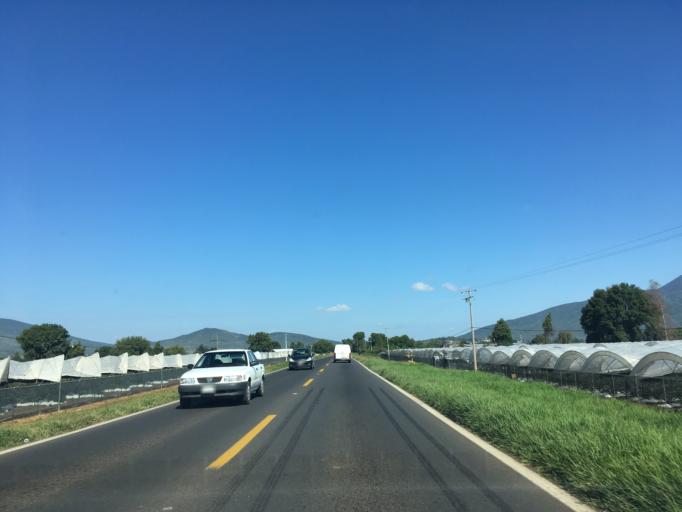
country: MX
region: Mexico
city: Tangancicuaro de Arista
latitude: 19.8667
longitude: -102.1916
